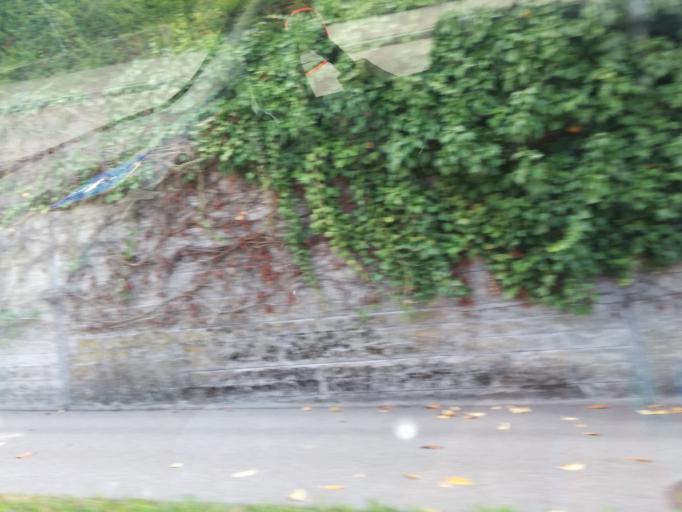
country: CH
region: Zurich
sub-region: Bezirk Meilen
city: Kuesnacht
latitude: 47.3226
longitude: 8.5827
